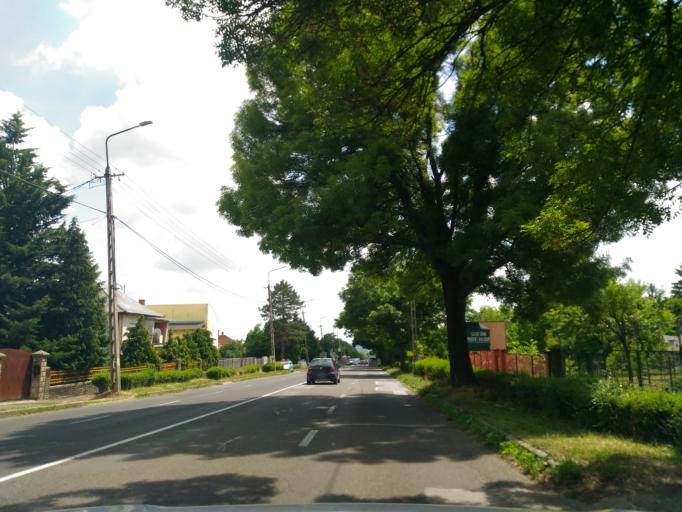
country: HU
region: Baranya
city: Pecs
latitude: 46.1052
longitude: 18.2641
